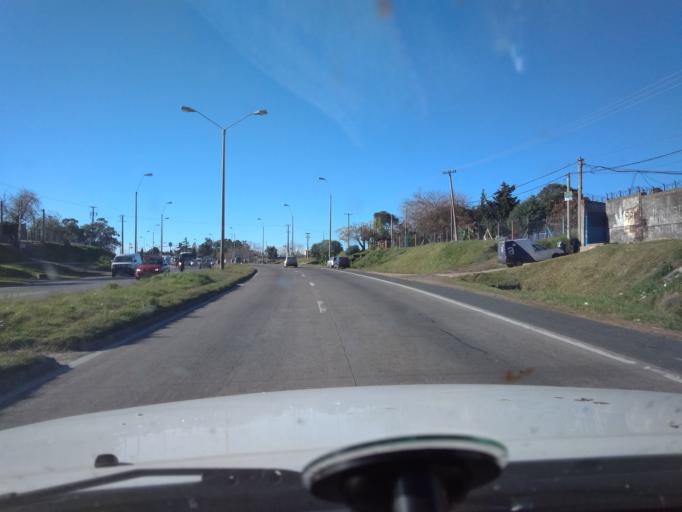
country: UY
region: Canelones
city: Colonia Nicolich
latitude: -34.7874
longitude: -56.0634
